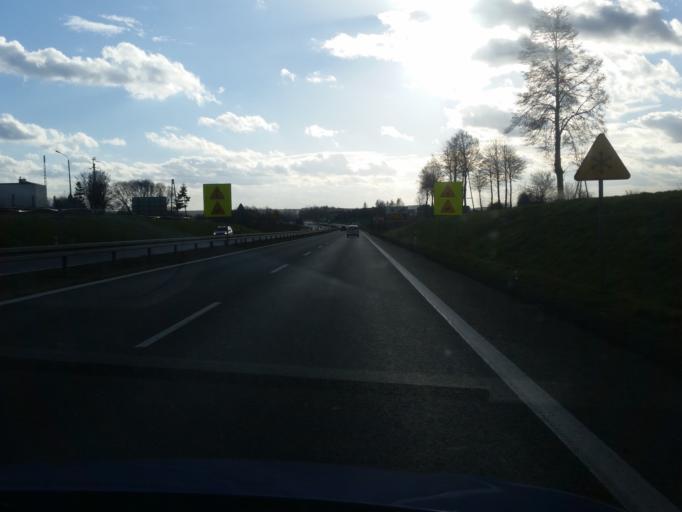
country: PL
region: Silesian Voivodeship
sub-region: Powiat myszkowski
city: Kozieglowy
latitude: 50.6028
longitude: 19.1521
